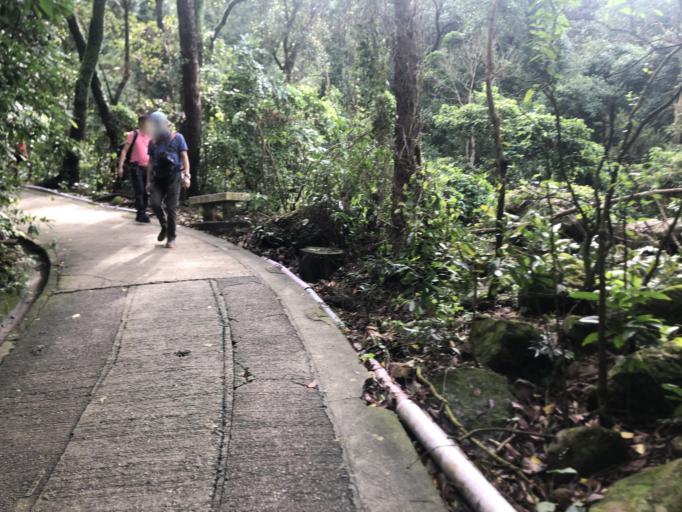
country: HK
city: Hong Kong
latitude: 22.2790
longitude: 114.1386
